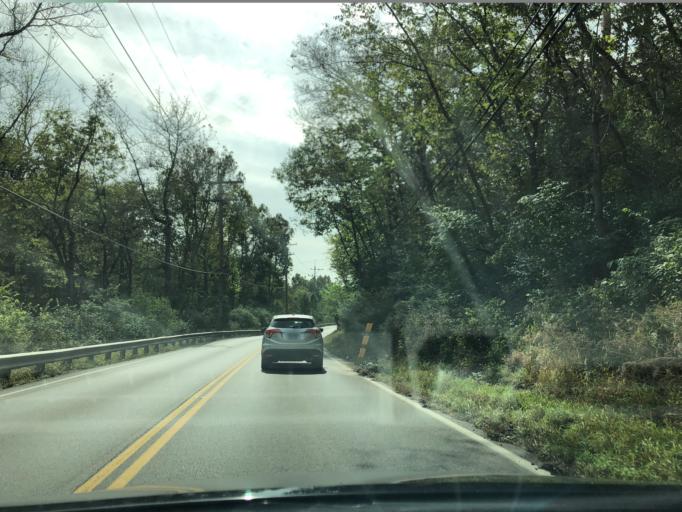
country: US
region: Ohio
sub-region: Clermont County
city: Milford
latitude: 39.1833
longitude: -84.2926
